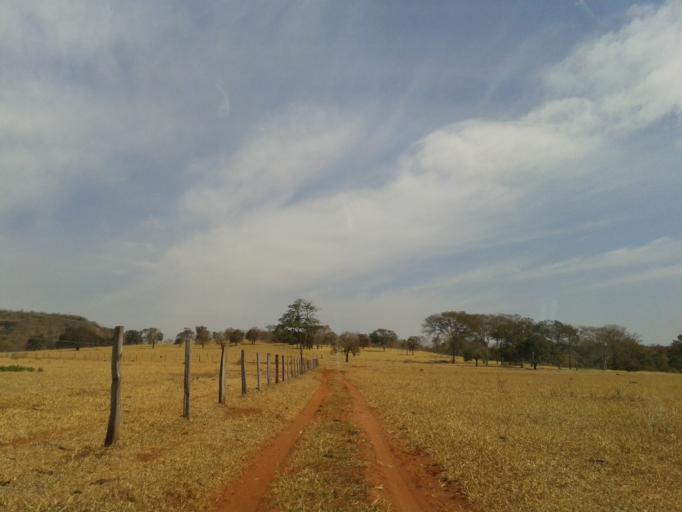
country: BR
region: Minas Gerais
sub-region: Santa Vitoria
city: Santa Vitoria
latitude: -19.2267
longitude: -50.0215
